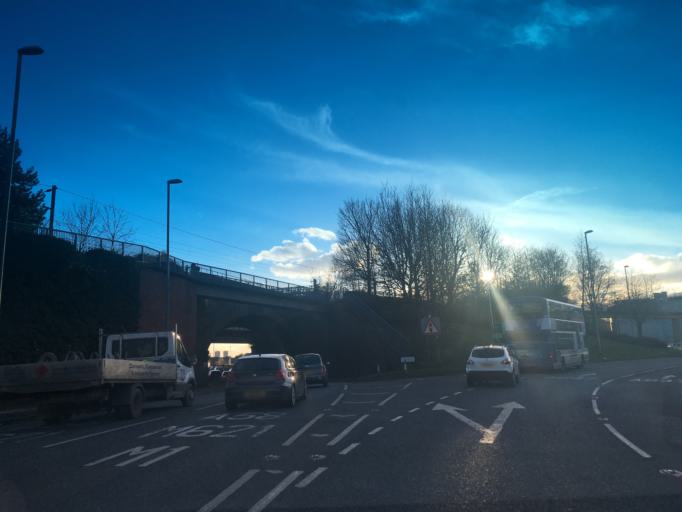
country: GB
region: England
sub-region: City and Borough of Leeds
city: Leeds
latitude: 53.7926
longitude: -1.5662
